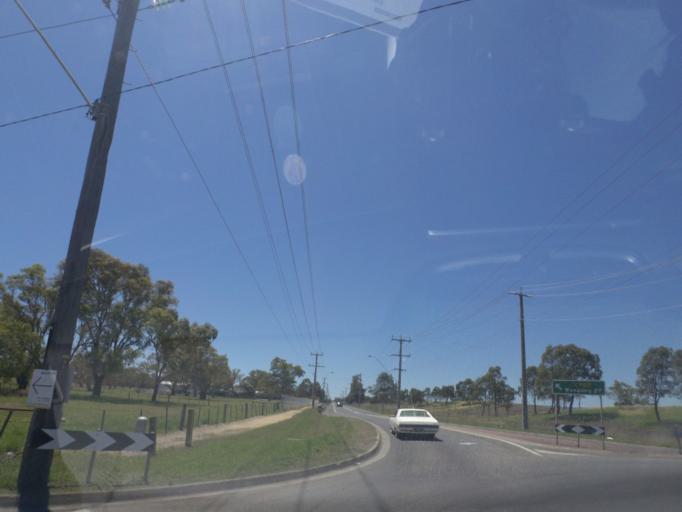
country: AU
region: Victoria
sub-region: Whittlesea
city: Epping
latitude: -37.5940
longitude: 145.0337
